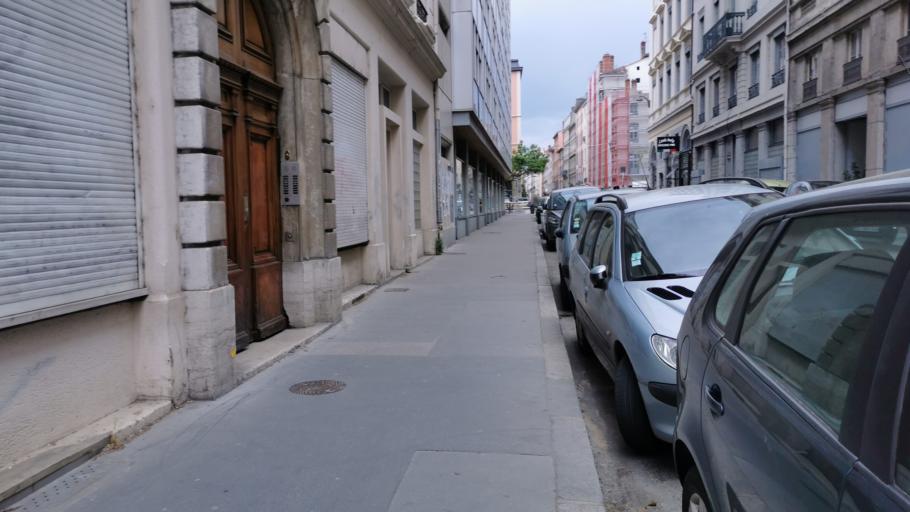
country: FR
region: Rhone-Alpes
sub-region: Departement du Rhone
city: Lyon
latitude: 45.7563
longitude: 4.8280
